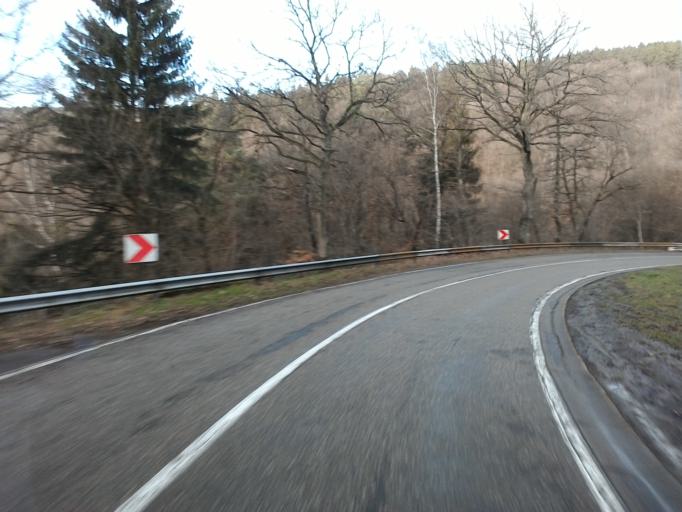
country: BE
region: Wallonia
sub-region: Province de Liege
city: Stoumont
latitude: 50.4146
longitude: 5.7915
